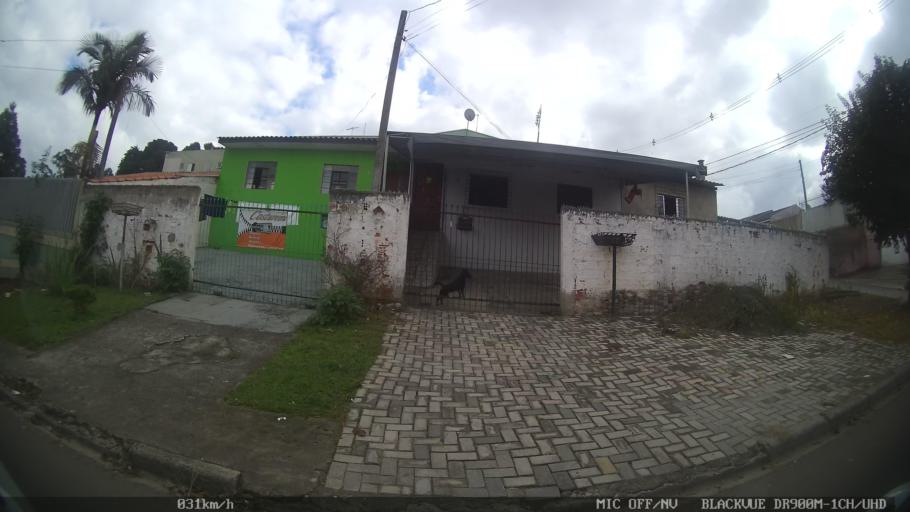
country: BR
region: Parana
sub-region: Colombo
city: Colombo
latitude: -25.3583
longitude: -49.2093
